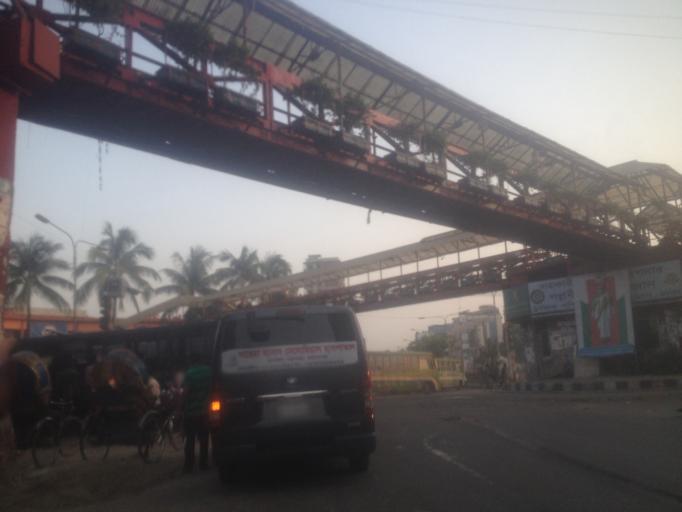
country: BD
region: Dhaka
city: Azimpur
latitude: 23.8066
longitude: 90.3687
